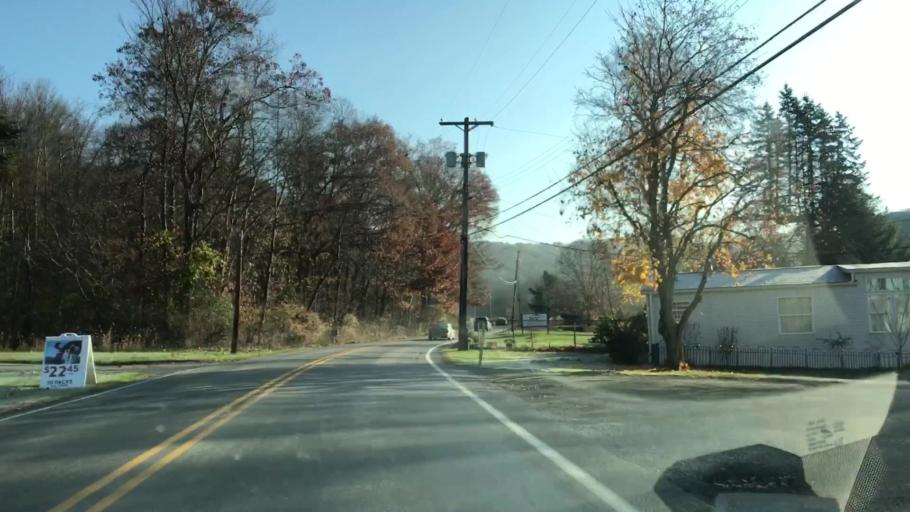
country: US
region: Pennsylvania
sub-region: Allegheny County
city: Bell Acres
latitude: 40.6135
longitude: -80.1491
